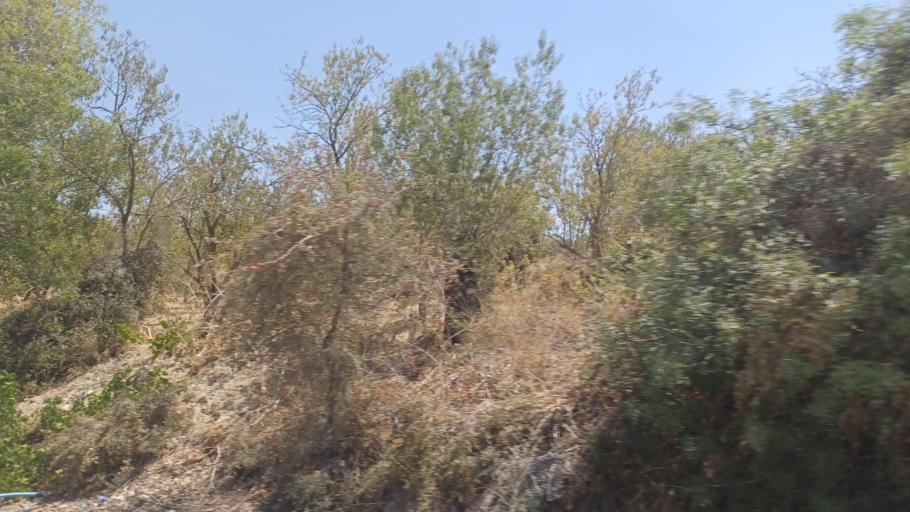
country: CY
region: Pafos
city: Mesogi
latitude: 34.8185
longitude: 32.4567
